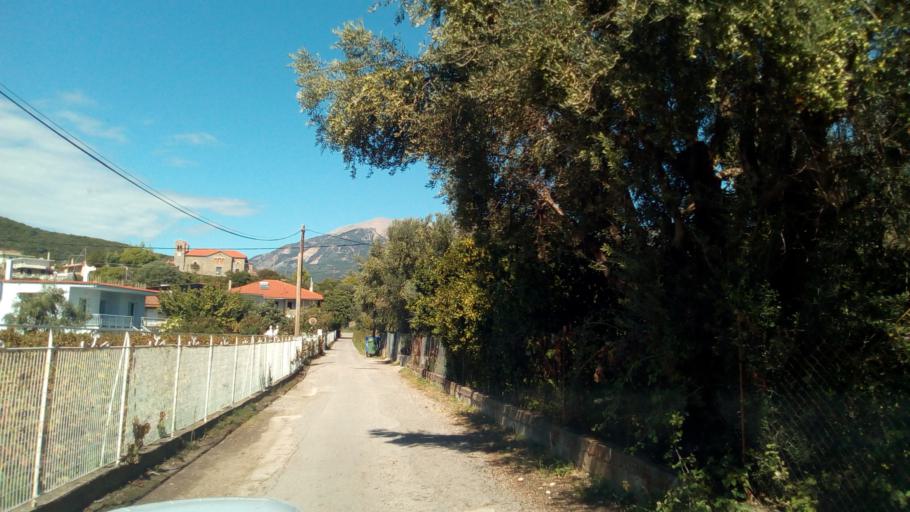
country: GR
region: West Greece
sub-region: Nomos Aitolias kai Akarnanias
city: Nafpaktos
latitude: 38.3785
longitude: 21.7989
